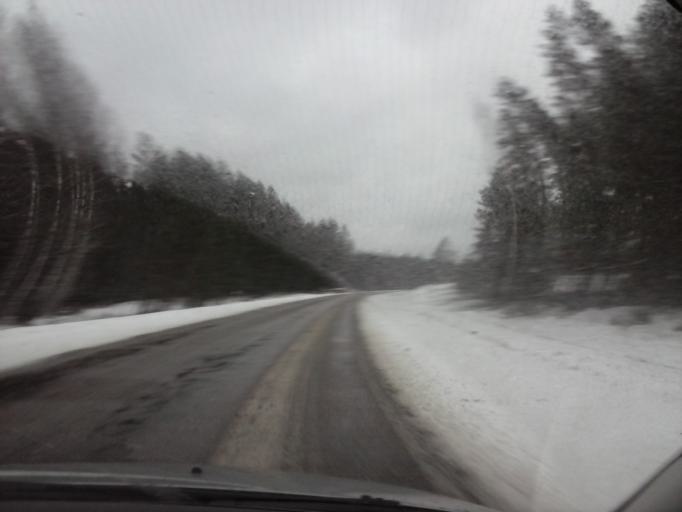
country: LV
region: Strenci
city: Seda
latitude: 57.6682
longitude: 25.8765
